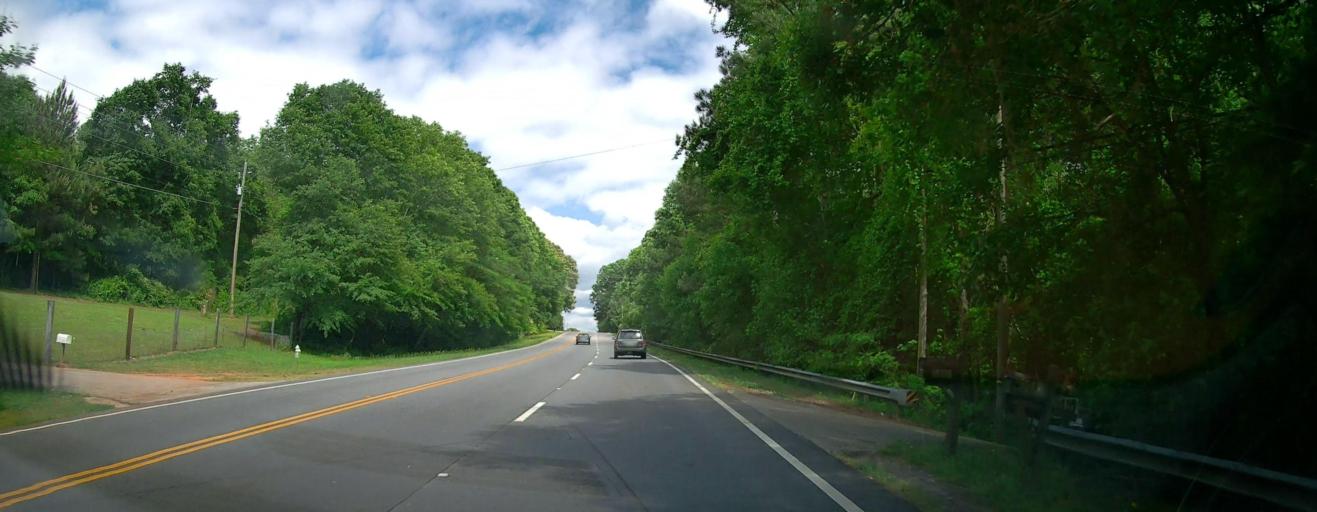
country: US
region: Georgia
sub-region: Rockdale County
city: Conyers
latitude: 33.6206
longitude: -84.0671
